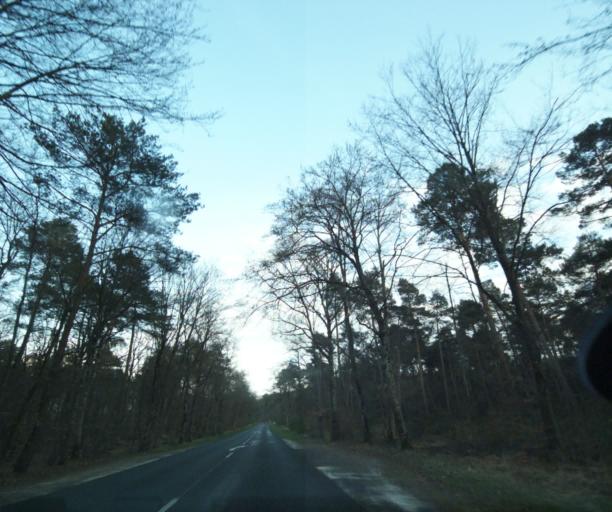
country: FR
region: Ile-de-France
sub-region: Departement de Seine-et-Marne
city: Avon
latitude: 48.3743
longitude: 2.7454
